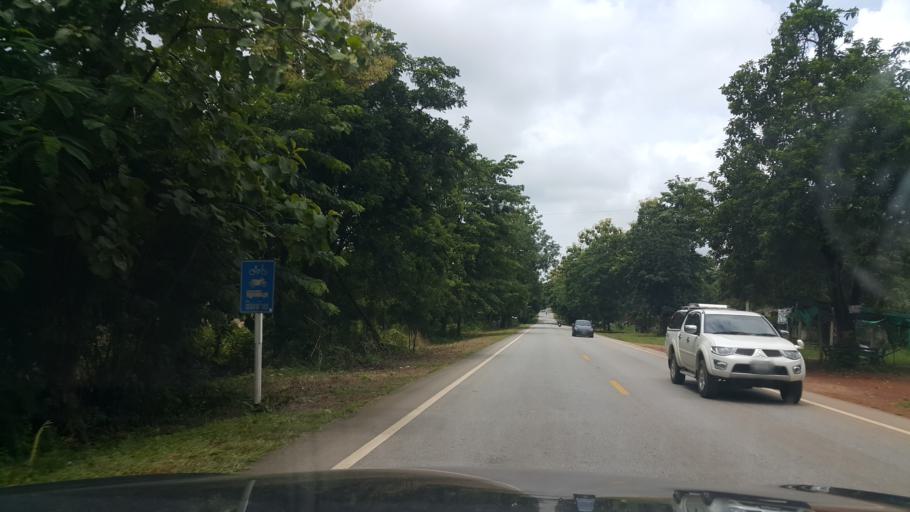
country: TH
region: Uttaradit
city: Lap Lae
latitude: 17.5751
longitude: 99.9491
